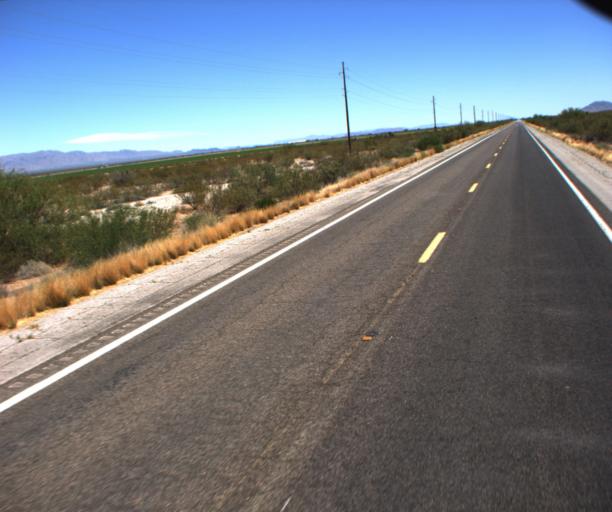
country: US
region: Arizona
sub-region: La Paz County
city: Salome
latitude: 33.8391
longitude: -113.4830
